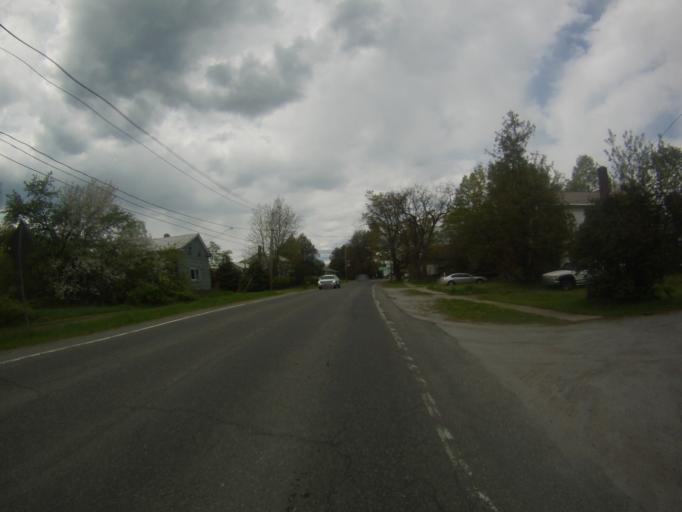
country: US
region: New York
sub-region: Essex County
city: Port Henry
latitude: 44.0474
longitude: -73.5060
